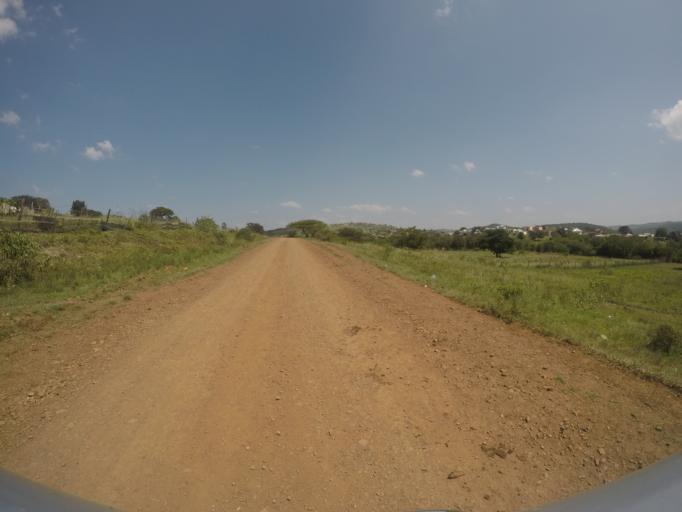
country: ZA
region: KwaZulu-Natal
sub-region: uThungulu District Municipality
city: Empangeni
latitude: -28.5927
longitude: 31.7362
